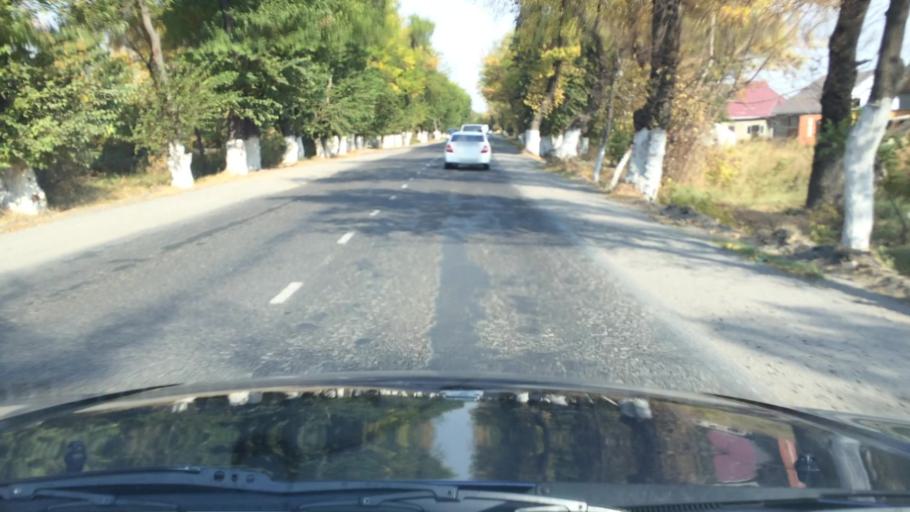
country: KG
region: Chuy
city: Lebedinovka
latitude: 42.9097
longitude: 74.6873
